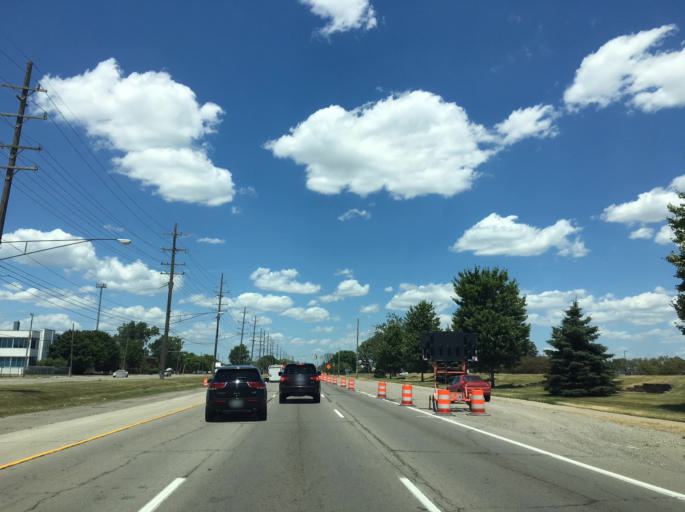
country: US
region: Michigan
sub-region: Macomb County
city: Warren
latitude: 42.4673
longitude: -83.0448
